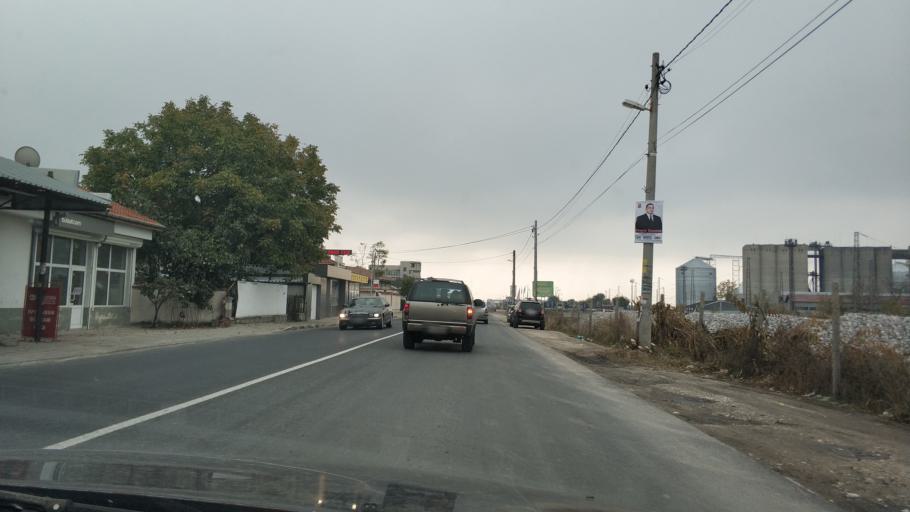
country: BG
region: Plovdiv
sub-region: Obshtina Plovdiv
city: Plovdiv
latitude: 42.2295
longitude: 24.7247
